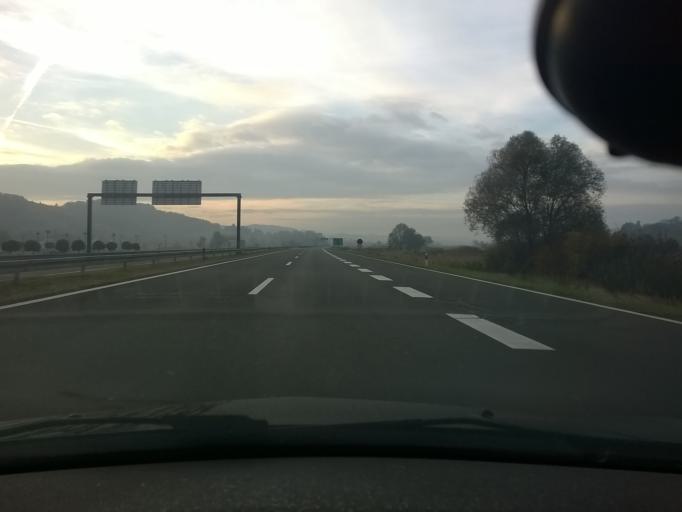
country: HR
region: Krapinsko-Zagorska
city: Zabok
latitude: 46.0875
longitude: 15.9101
